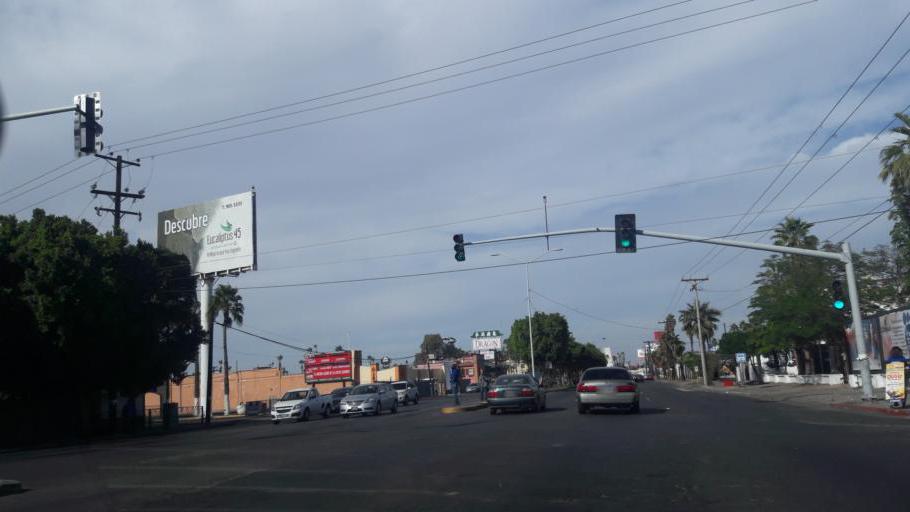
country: MX
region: Baja California
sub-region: Mexicali
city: Mexicali
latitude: 32.6440
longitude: -115.4509
